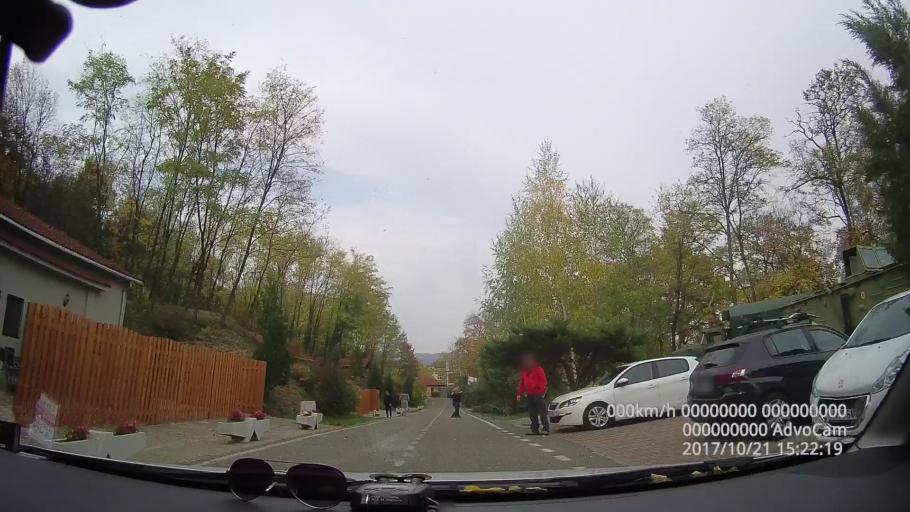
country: RO
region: Hunedoara
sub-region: Municipiul Deva
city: Cristur
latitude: 45.8548
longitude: 22.9602
